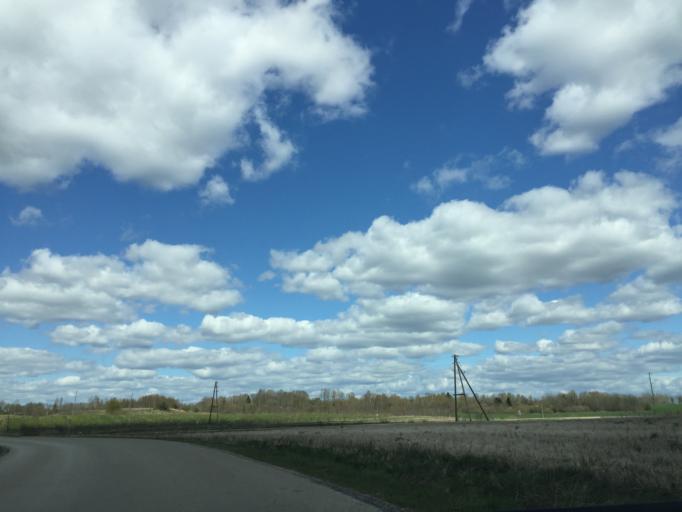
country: LV
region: Rezekne
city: Rezekne
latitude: 56.5507
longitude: 27.1508
